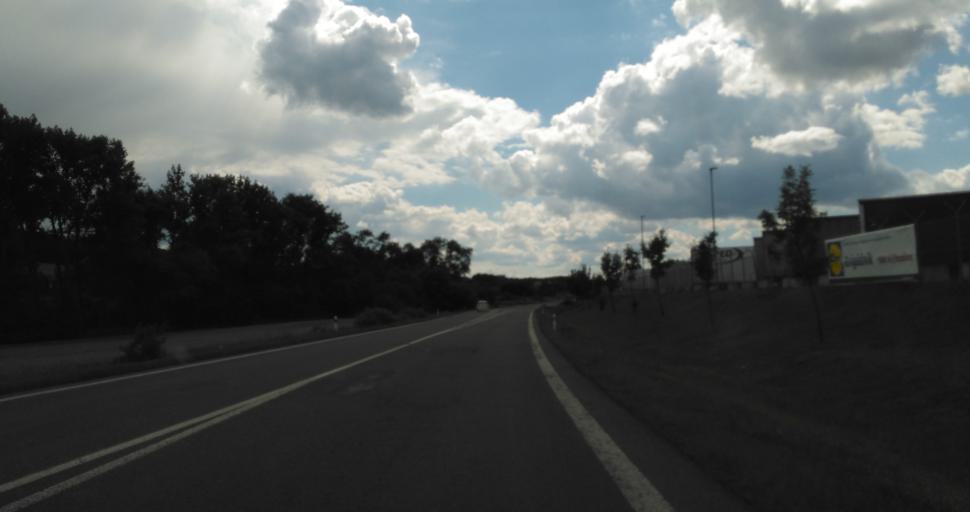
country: CZ
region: Central Bohemia
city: Komarov
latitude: 49.8437
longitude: 13.8215
